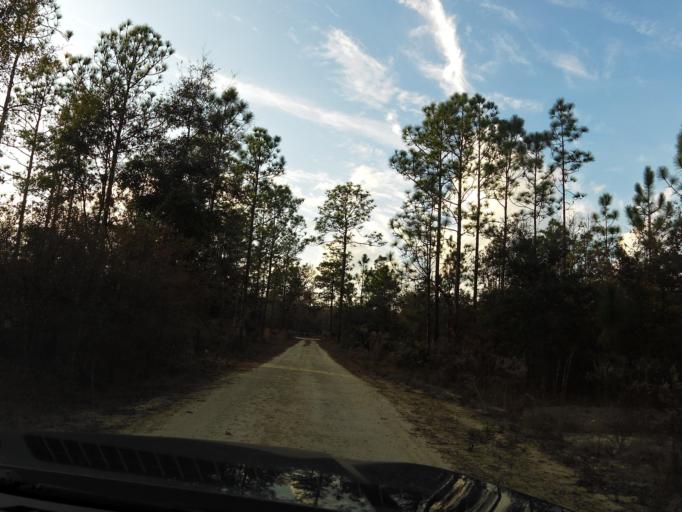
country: US
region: Florida
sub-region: Clay County
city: Middleburg
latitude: 30.1321
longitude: -81.9481
